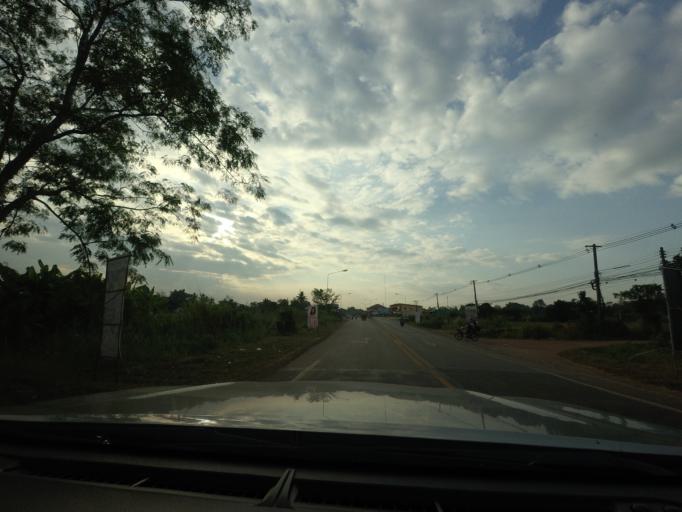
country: TH
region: Phitsanulok
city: Noen Maprang
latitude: 16.5693
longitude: 100.6452
